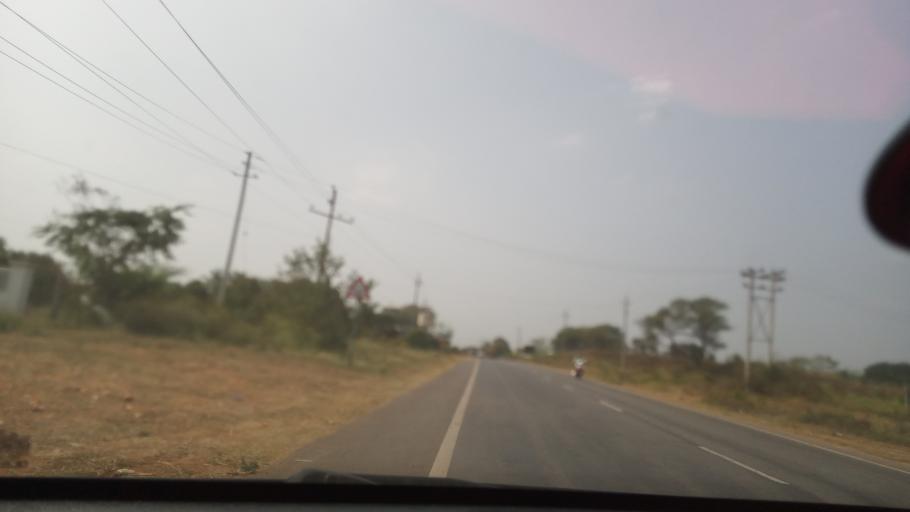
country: IN
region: Karnataka
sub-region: Chamrajnagar
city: Chamrajnagar
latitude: 11.9968
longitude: 76.8518
